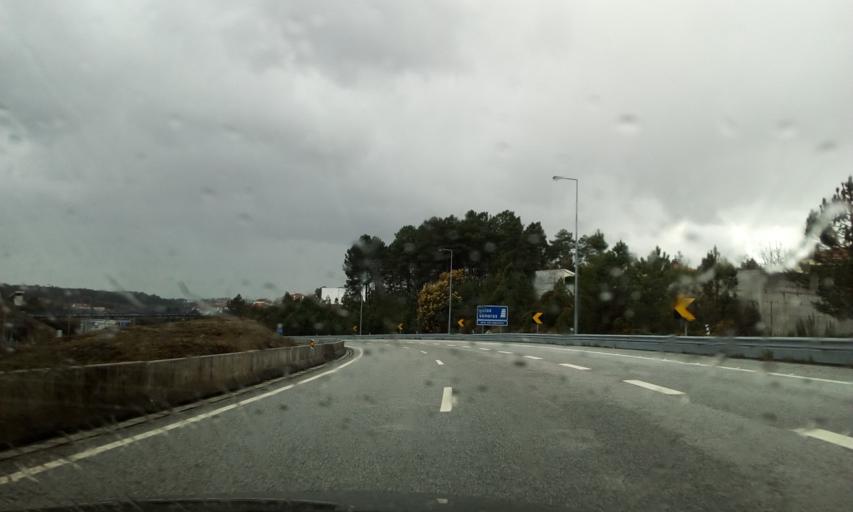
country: PT
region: Viseu
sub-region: Viseu
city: Rio de Loba
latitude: 40.6539
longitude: -7.8663
